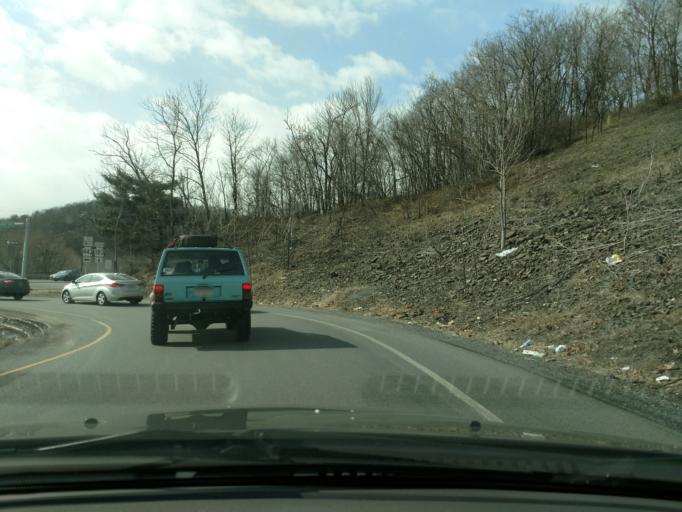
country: US
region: Pennsylvania
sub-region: Schuylkill County
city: Schuylkill Haven
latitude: 40.6377
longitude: -76.1818
